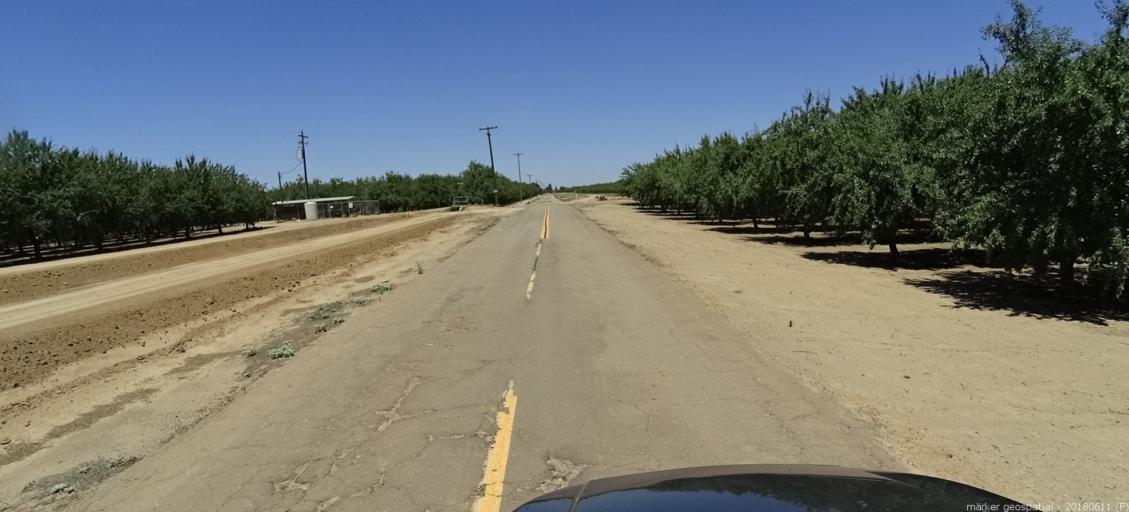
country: US
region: California
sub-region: Madera County
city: Fairmead
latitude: 37.0466
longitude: -120.1933
